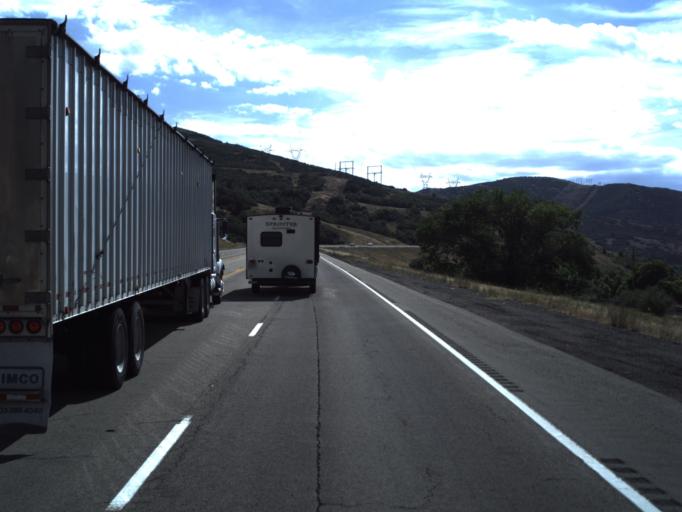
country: US
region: Utah
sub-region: Utah County
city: Mapleton
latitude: 40.0344
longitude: -111.5217
